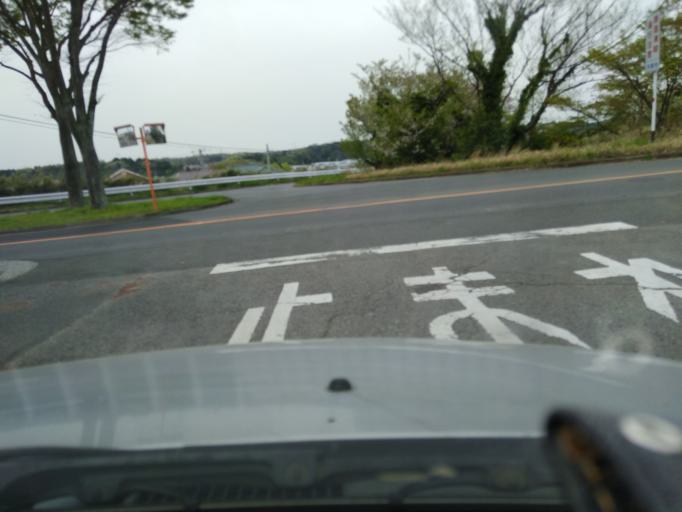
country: JP
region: Chiba
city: Ichihara
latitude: 35.4499
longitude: 140.0554
